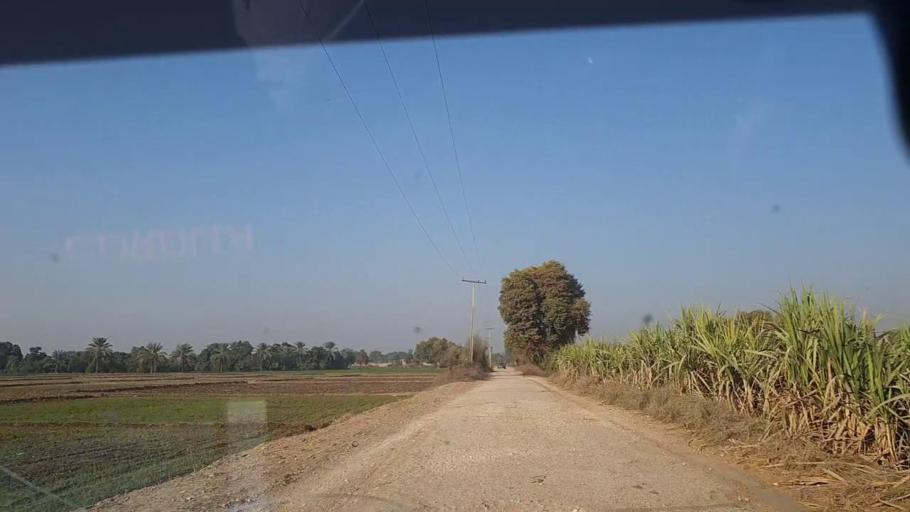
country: PK
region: Sindh
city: Sobhadero
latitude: 27.2502
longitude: 68.3501
